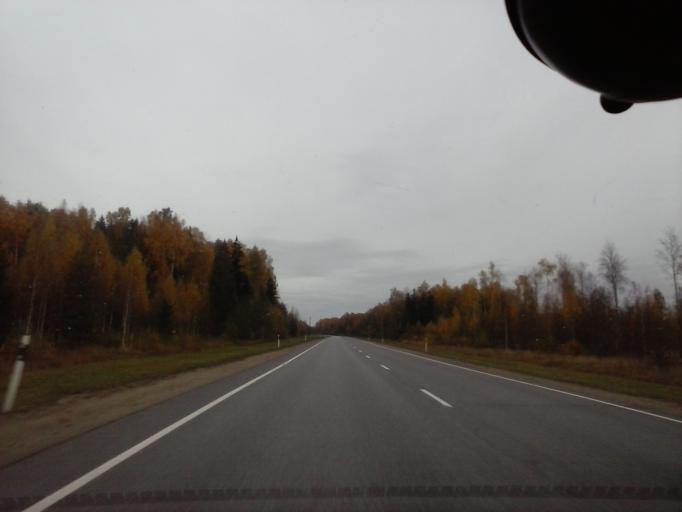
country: EE
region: Tartu
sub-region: Puhja vald
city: Puhja
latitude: 58.4973
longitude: 26.3313
